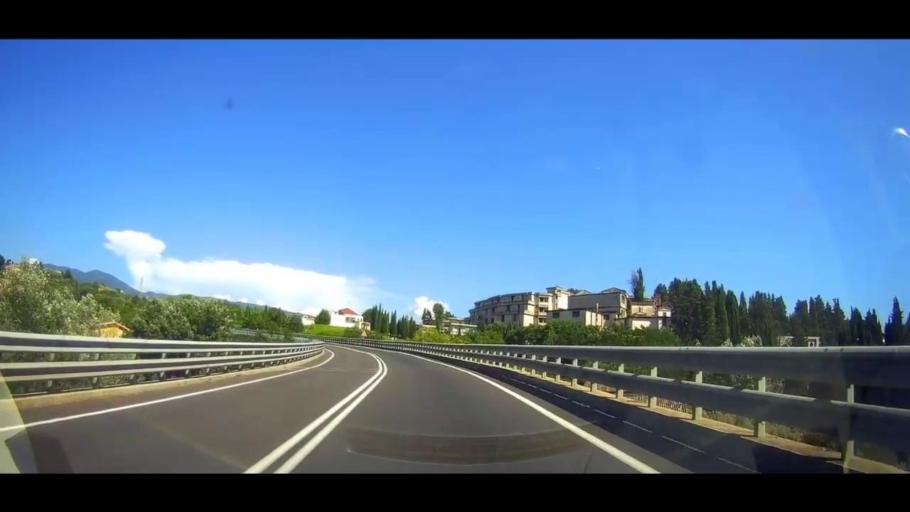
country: IT
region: Calabria
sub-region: Provincia di Cosenza
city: Cosenza
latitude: 39.2956
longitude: 16.2665
